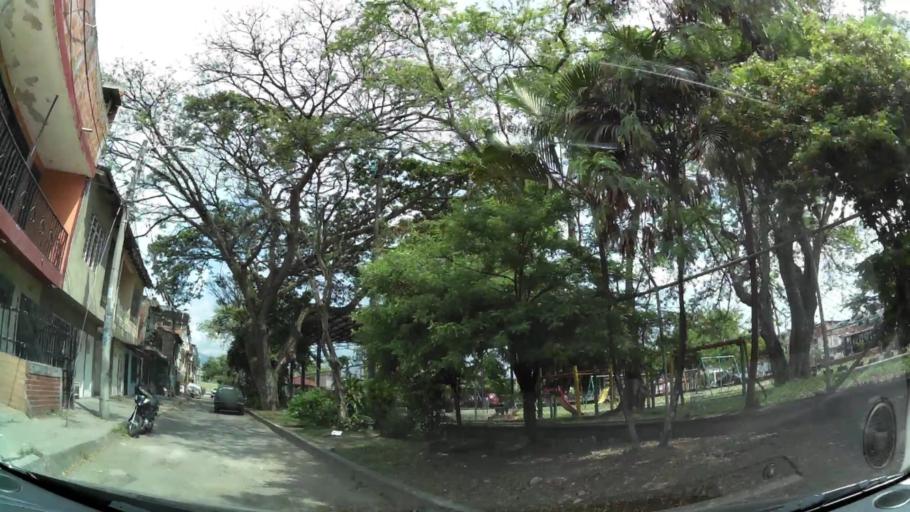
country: CO
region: Valle del Cauca
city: Cali
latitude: 3.4897
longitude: -76.4892
